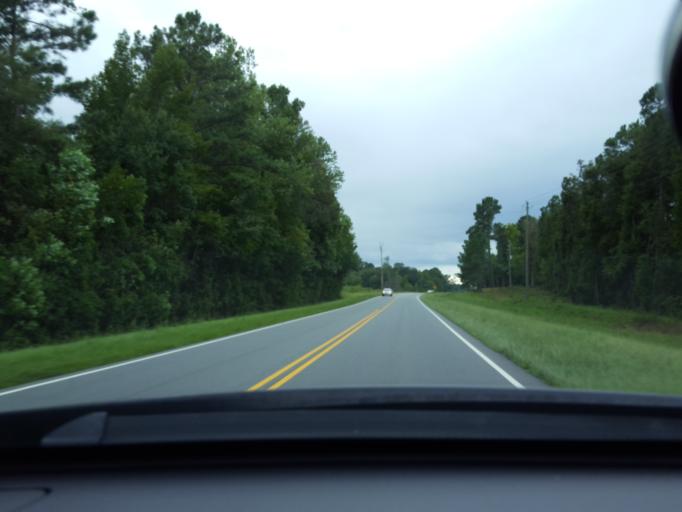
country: US
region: North Carolina
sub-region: Sampson County
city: Roseboro
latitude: 34.7522
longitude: -78.4186
